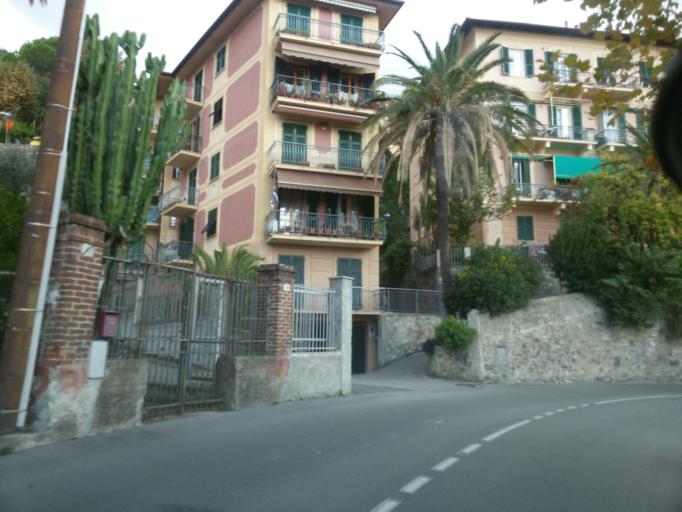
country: IT
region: Liguria
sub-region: Provincia di Genova
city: Camogli
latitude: 44.3477
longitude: 9.1587
